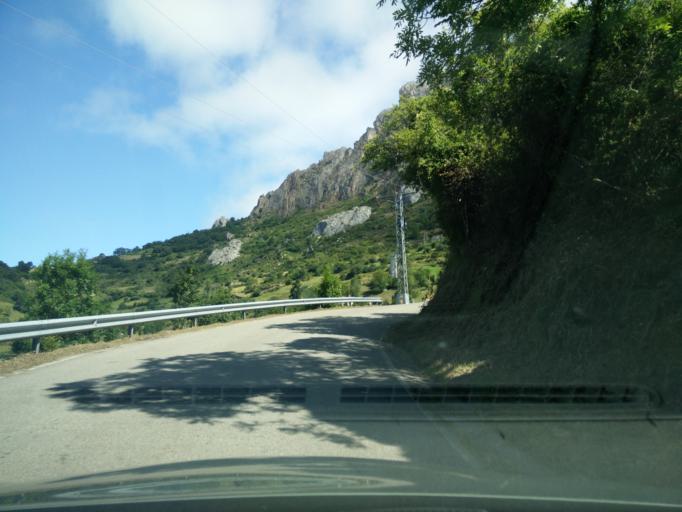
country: ES
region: Asturias
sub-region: Province of Asturias
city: Pola de Somiedo
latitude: 43.0862
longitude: -6.2363
